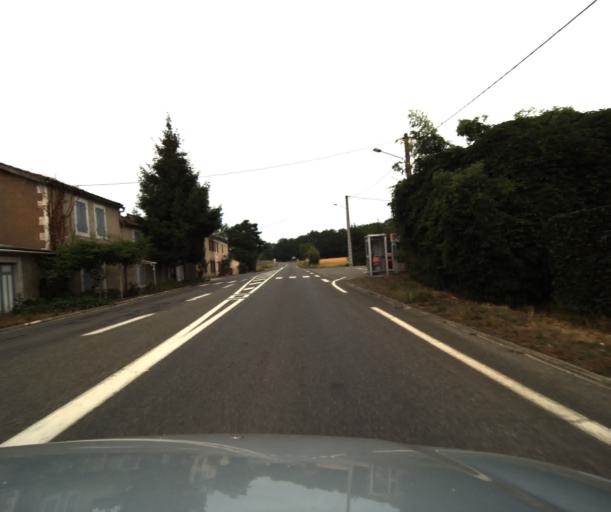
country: FR
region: Midi-Pyrenees
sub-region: Departement du Gers
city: Mielan
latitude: 43.4701
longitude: 0.3277
